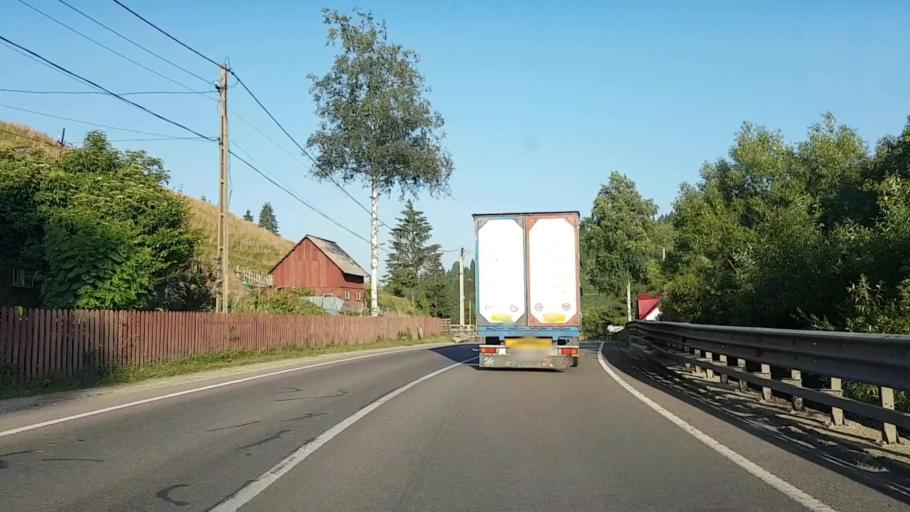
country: RO
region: Suceava
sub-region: Comuna Dorna Candrenilor
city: Dorna Candrenilor
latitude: 47.3566
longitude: 25.2796
